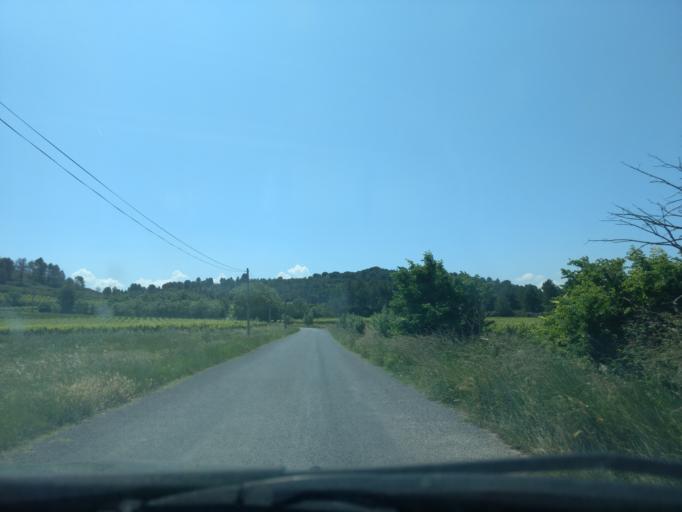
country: FR
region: Languedoc-Roussillon
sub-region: Departement de l'Aude
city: Canet
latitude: 43.2661
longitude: 2.8158
